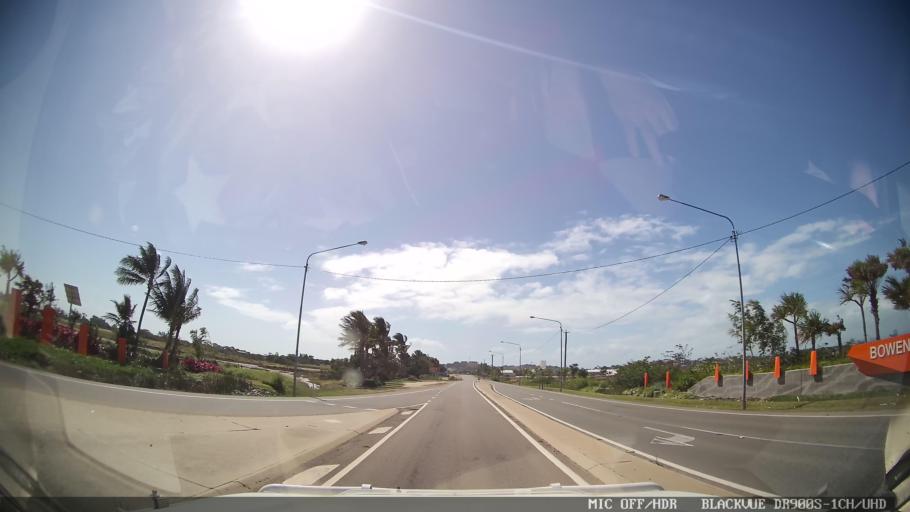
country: AU
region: Queensland
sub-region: Whitsunday
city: Bowen
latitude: -20.0150
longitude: 148.2216
